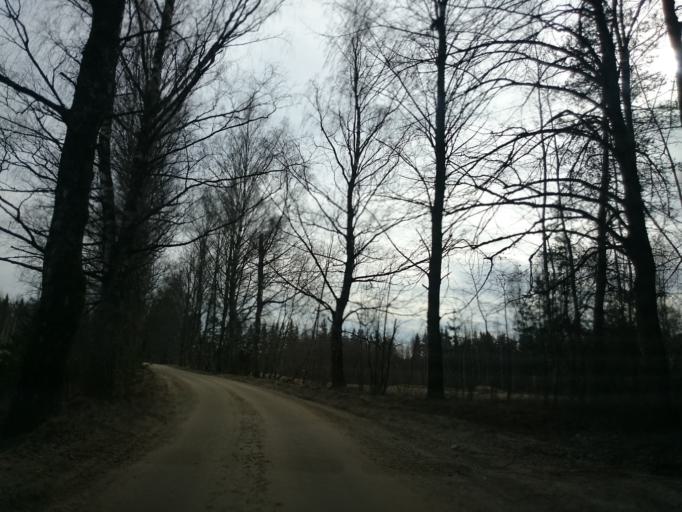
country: LV
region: Garkalne
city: Garkalne
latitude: 57.0184
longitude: 24.3863
